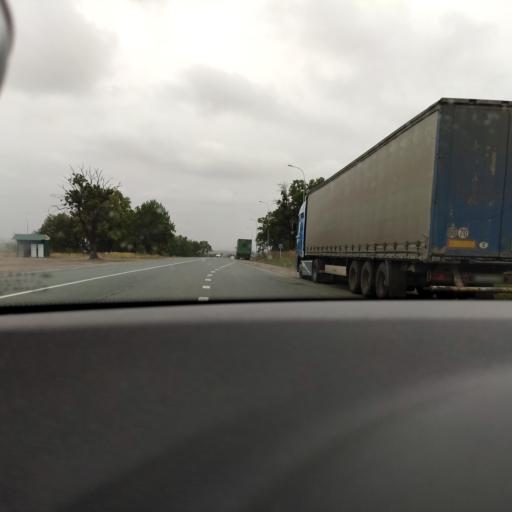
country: RU
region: Samara
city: Mirnyy
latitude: 53.5853
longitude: 50.2841
